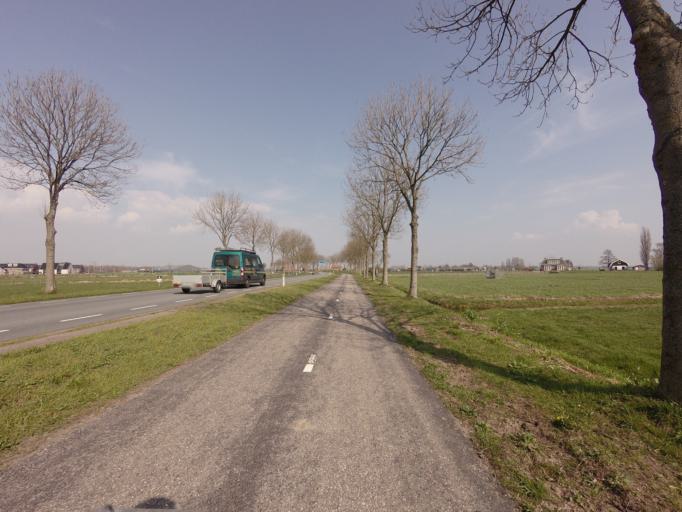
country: NL
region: Utrecht
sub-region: Stichtse Vecht
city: Vreeland
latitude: 52.2460
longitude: 5.0515
